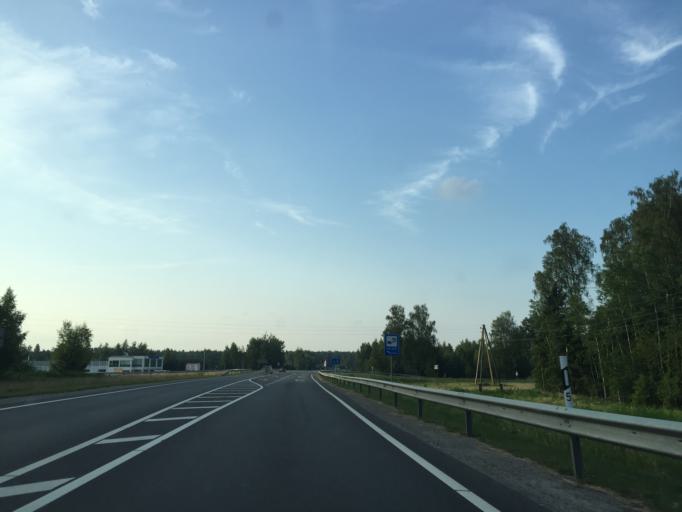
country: LV
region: Ozolnieku
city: Ozolnieki
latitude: 56.6866
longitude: 23.8210
